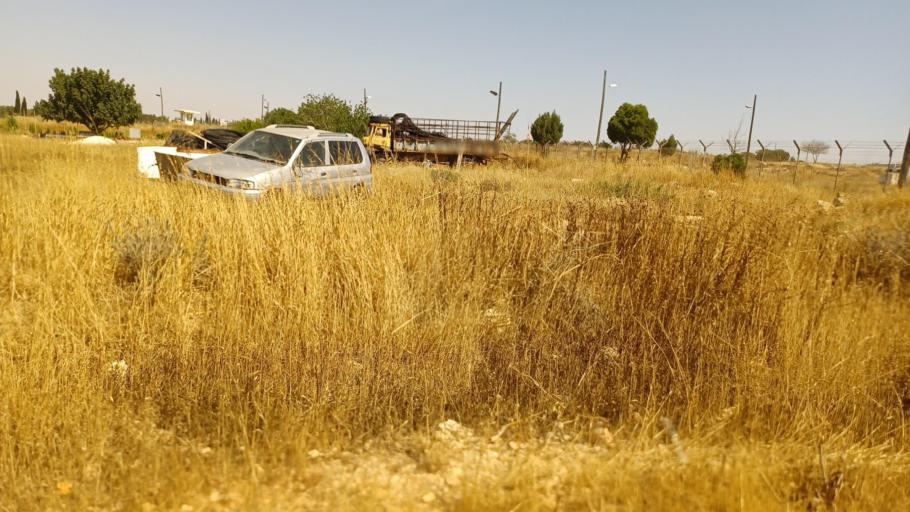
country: CY
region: Ammochostos
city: Frenaros
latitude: 35.0245
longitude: 33.9219
